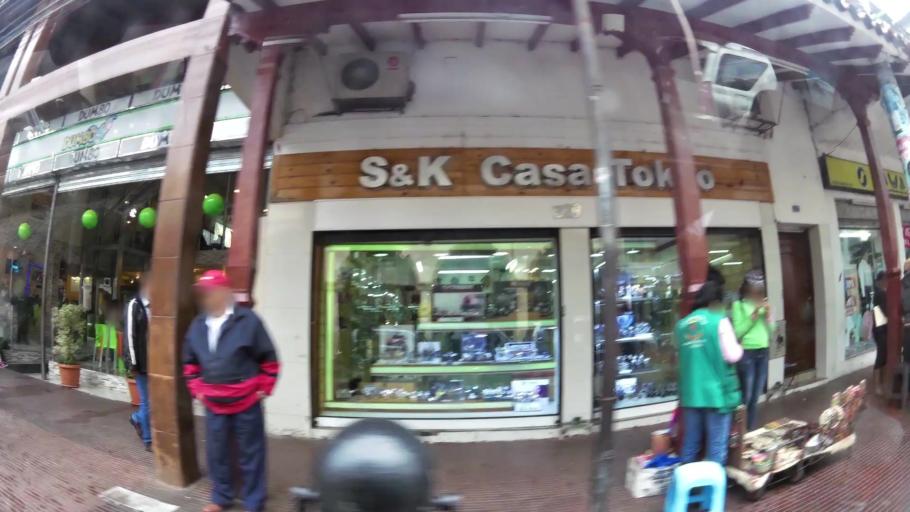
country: BO
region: Santa Cruz
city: Santa Cruz de la Sierra
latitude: -17.7839
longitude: -63.1840
